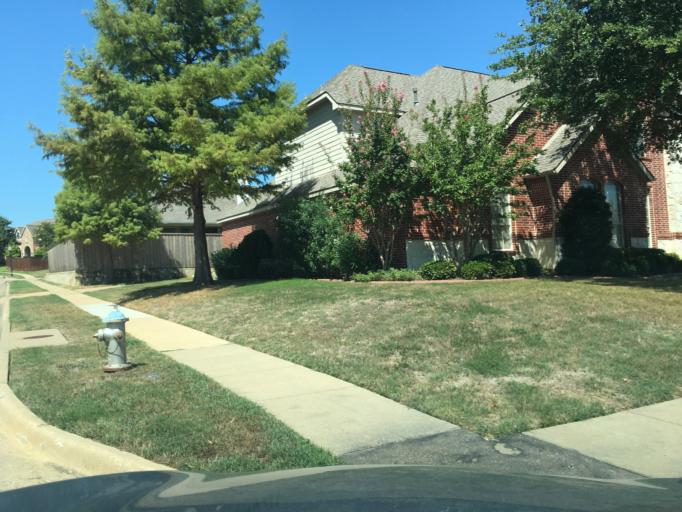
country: US
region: Texas
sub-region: Dallas County
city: Sachse
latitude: 32.9600
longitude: -96.6205
